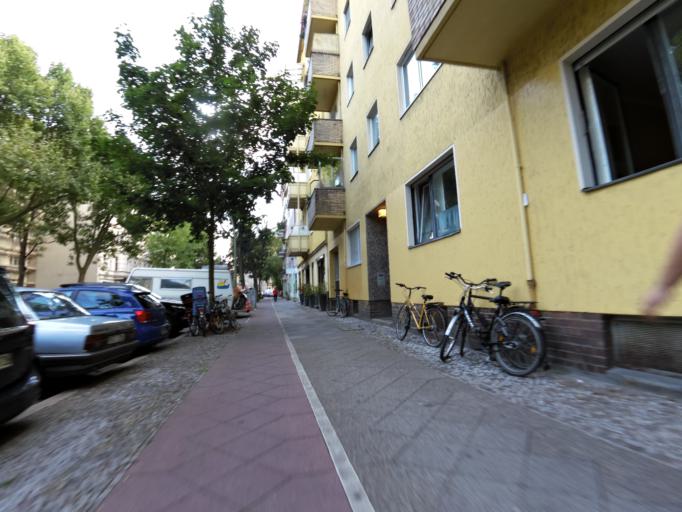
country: DE
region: Berlin
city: Berlin Schoeneberg
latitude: 52.4910
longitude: 13.3548
